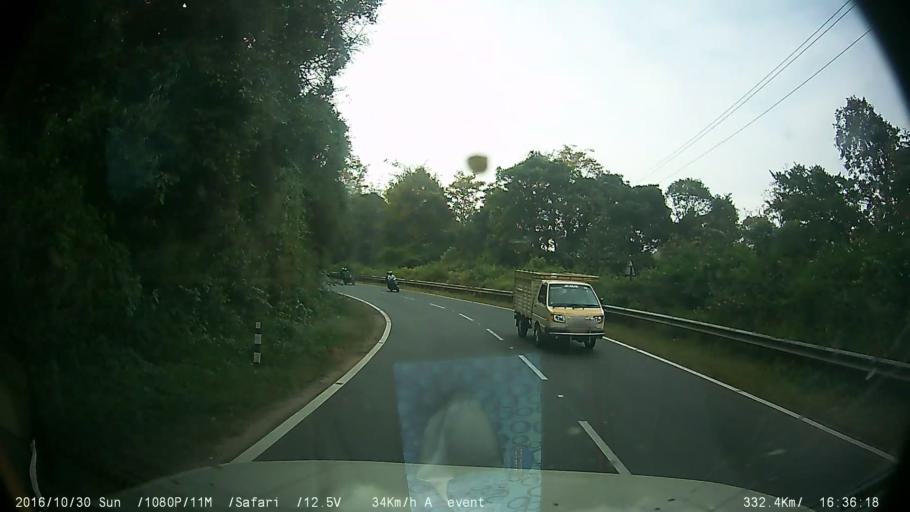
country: IN
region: Karnataka
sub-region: Kodagu
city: Madikeri
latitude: 12.4276
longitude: 75.7604
